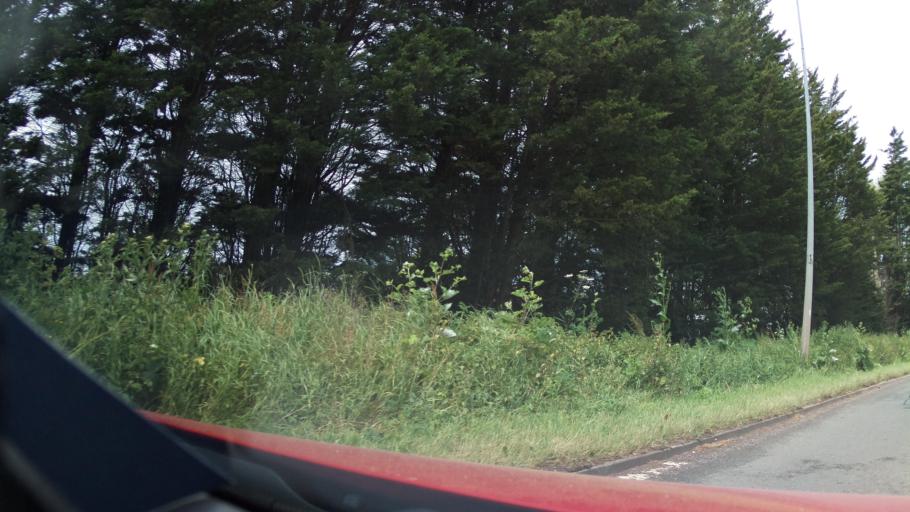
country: GB
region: Wales
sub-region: Vale of Glamorgan
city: Dinas Powys
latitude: 51.4085
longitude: -3.2276
